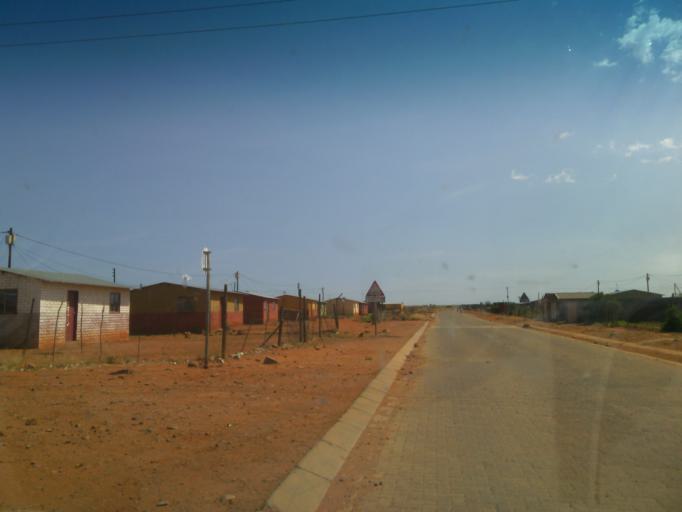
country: ZA
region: Northern Cape
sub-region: Frances Baard District Municipality
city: Barkly West
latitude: -28.5240
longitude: 24.5010
